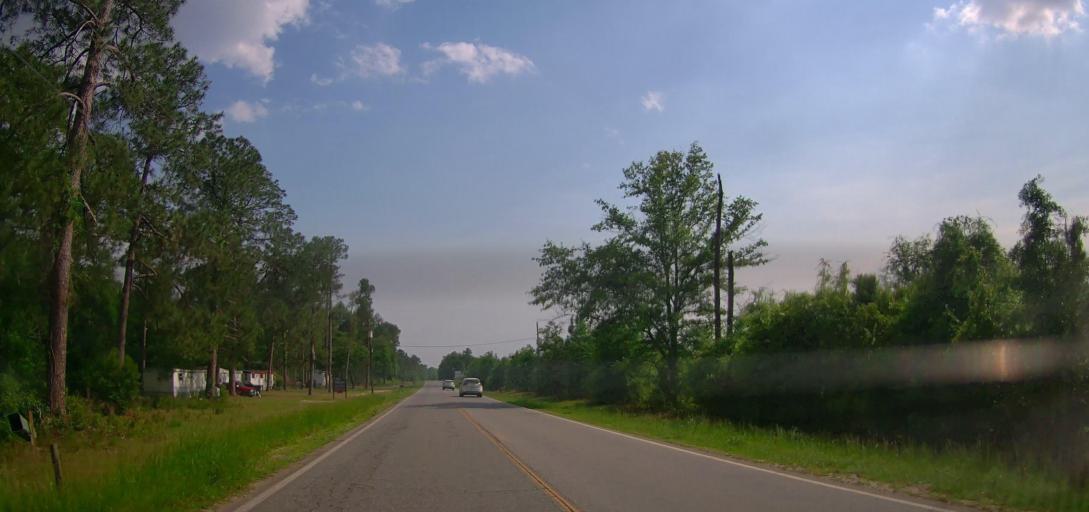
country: US
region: Georgia
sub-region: Laurens County
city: East Dublin
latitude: 32.5889
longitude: -82.8649
